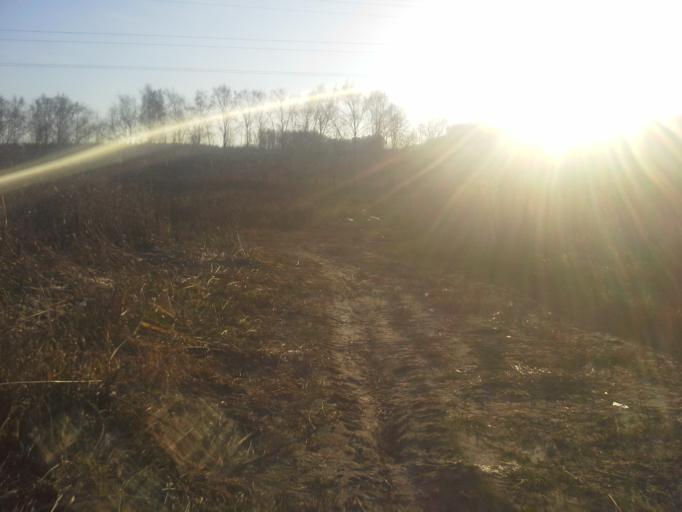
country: RU
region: Moskovskaya
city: Lesnoy Gorodok
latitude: 55.6536
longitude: 37.1848
